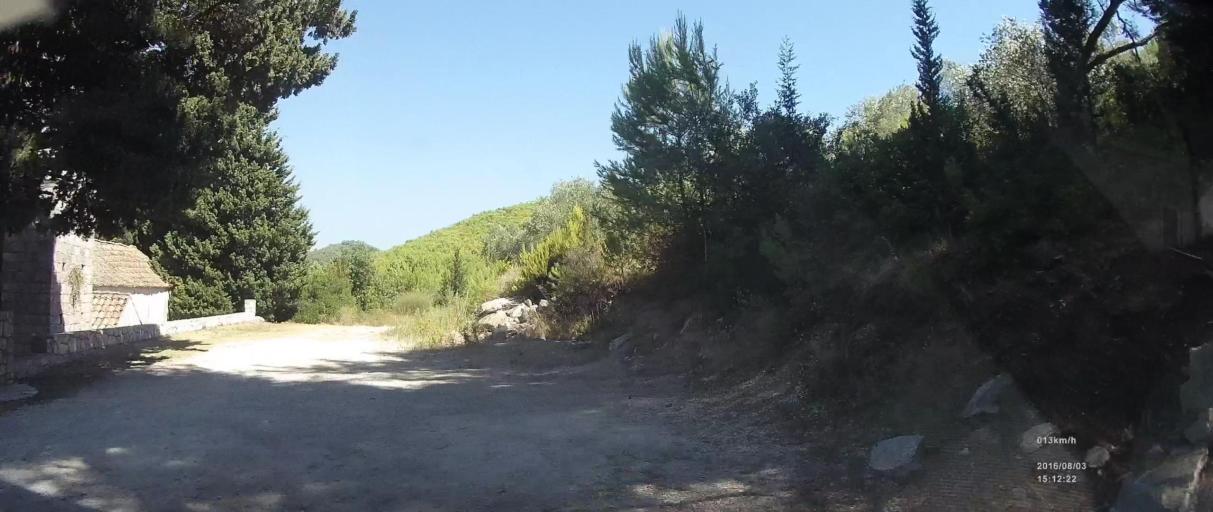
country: HR
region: Dubrovacko-Neretvanska
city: Blato
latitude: 42.7287
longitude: 17.5570
